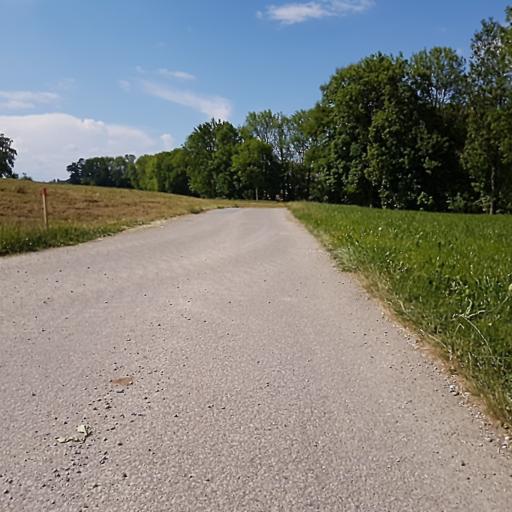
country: CH
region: Thurgau
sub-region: Arbon District
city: Amriswil
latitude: 47.5589
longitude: 9.3000
